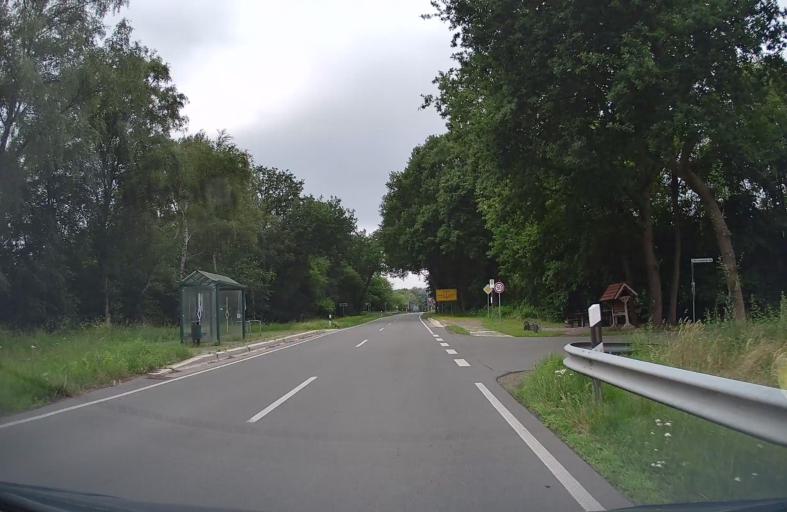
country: DE
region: Lower Saxony
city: Friesoythe
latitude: 53.0563
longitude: 7.8059
